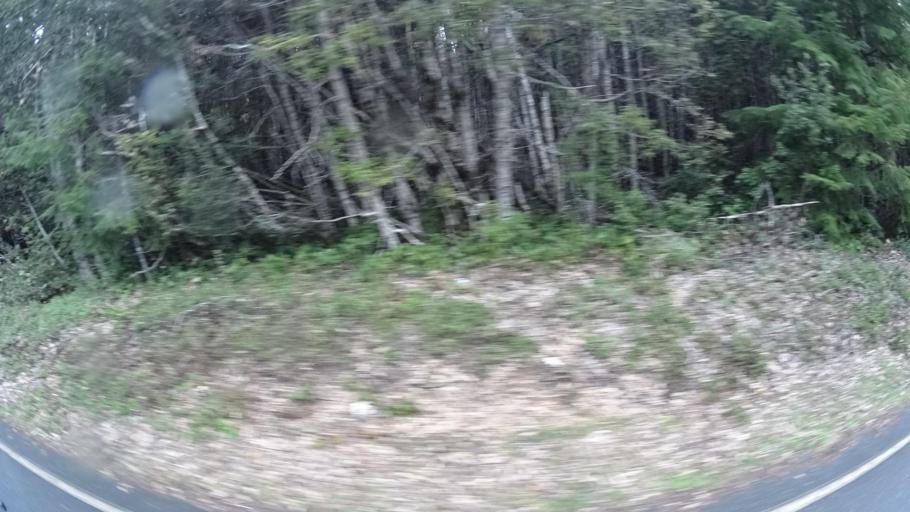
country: US
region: California
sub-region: Humboldt County
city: Willow Creek
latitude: 41.1925
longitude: -123.8136
